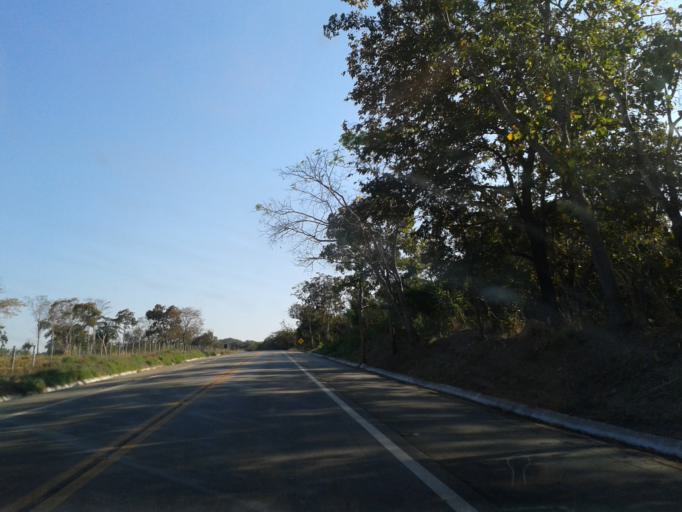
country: BR
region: Goias
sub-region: Itapirapua
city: Itapirapua
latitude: -15.3110
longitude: -50.4431
